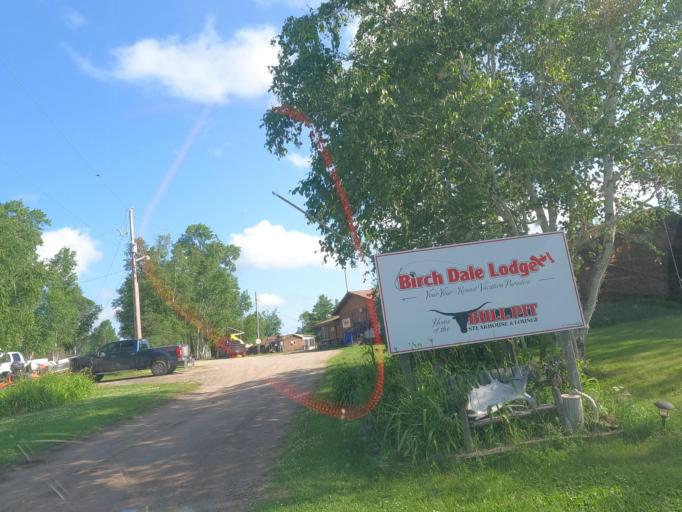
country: CA
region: Ontario
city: Dryden
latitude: 49.8230
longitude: -93.3387
